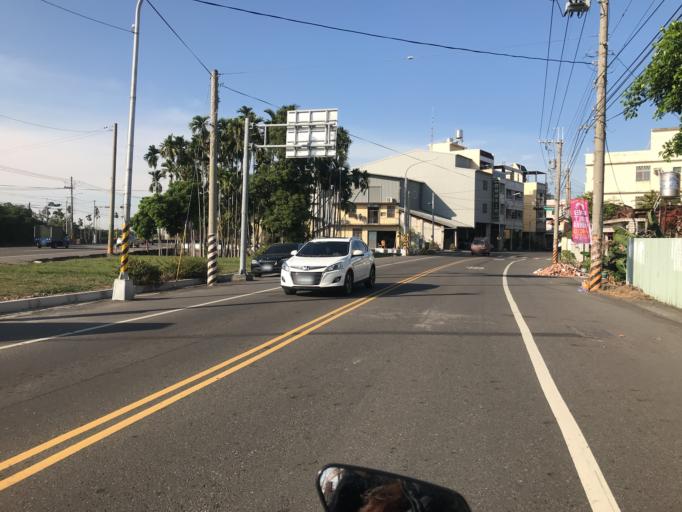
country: TW
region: Taiwan
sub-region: Nantou
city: Nantou
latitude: 23.8864
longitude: 120.5864
